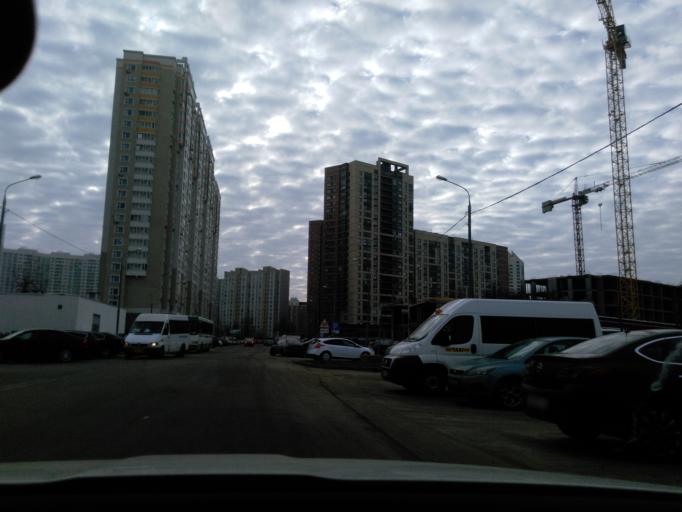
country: RU
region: Moskovskaya
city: Levoberezhnaya
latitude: 55.8995
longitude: 37.4745
